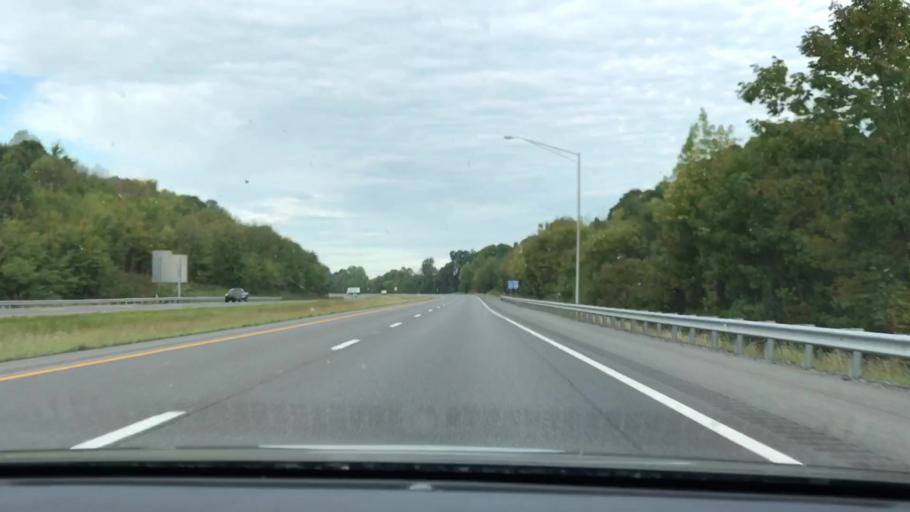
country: US
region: Kentucky
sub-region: Lyon County
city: Eddyville
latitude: 37.0755
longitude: -88.1273
